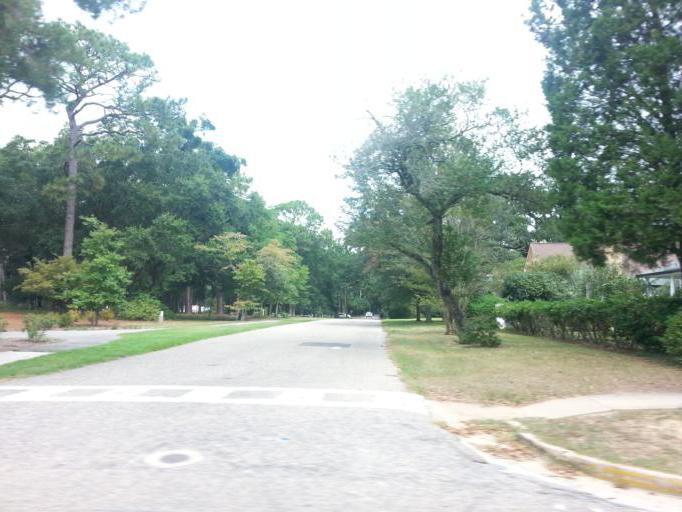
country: US
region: Alabama
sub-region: Baldwin County
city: Fairhope
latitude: 30.5231
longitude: -87.9082
